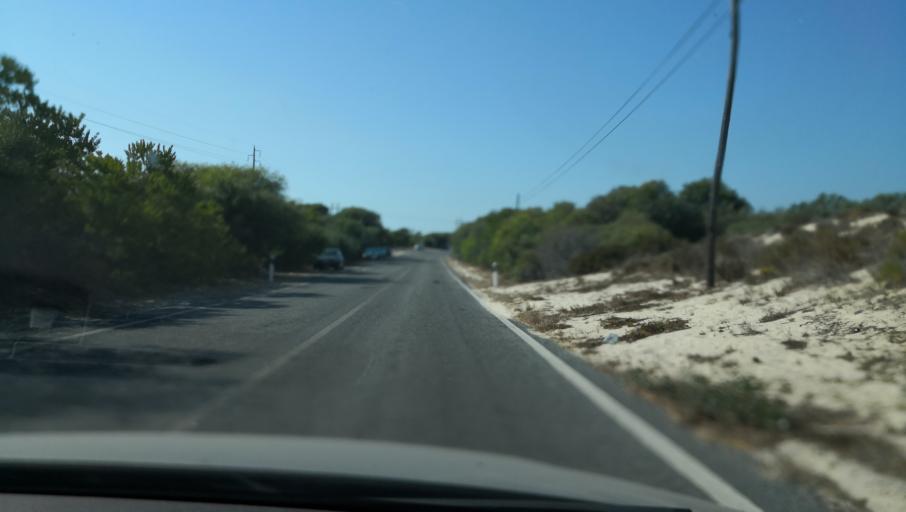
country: PT
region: Setubal
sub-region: Setubal
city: Setubal
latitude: 38.4185
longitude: -8.8181
